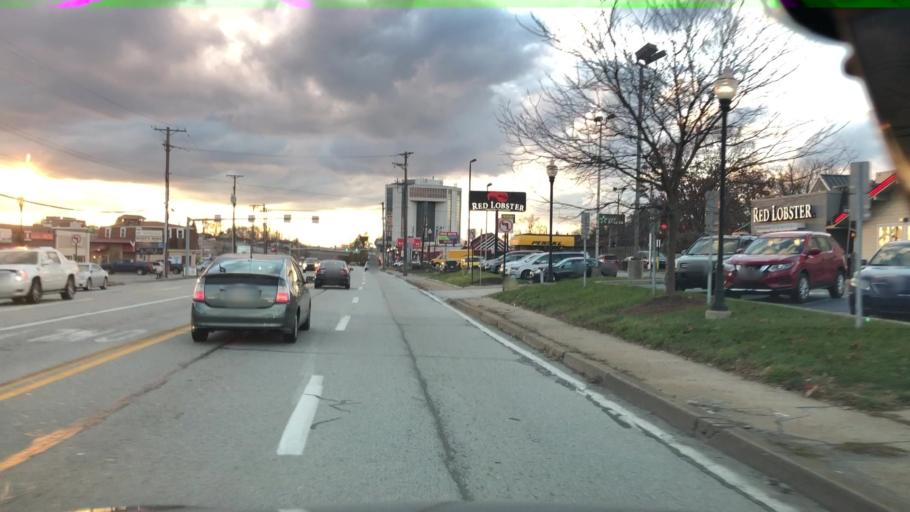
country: US
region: Pennsylvania
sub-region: Allegheny County
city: Monroeville
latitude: 40.4382
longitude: -79.7746
